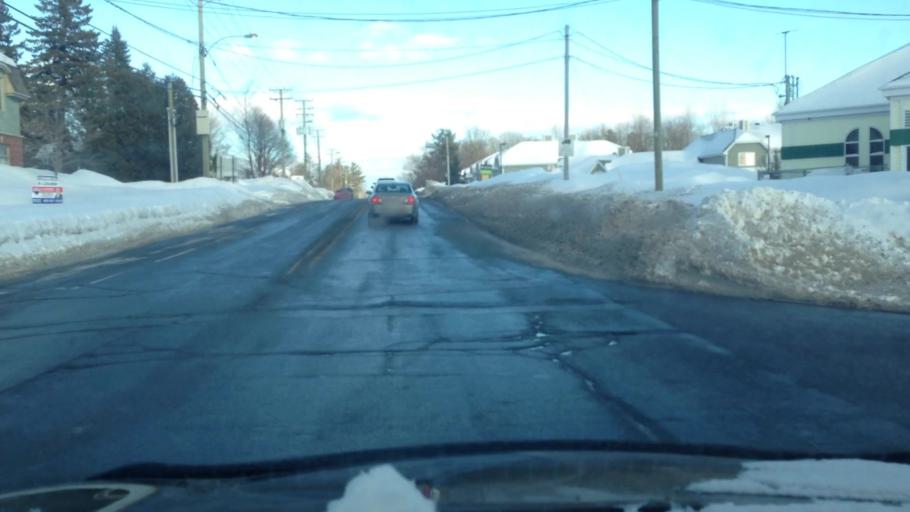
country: CA
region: Quebec
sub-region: Laurentides
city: Saint-Jerome
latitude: 45.7957
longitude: -73.9953
